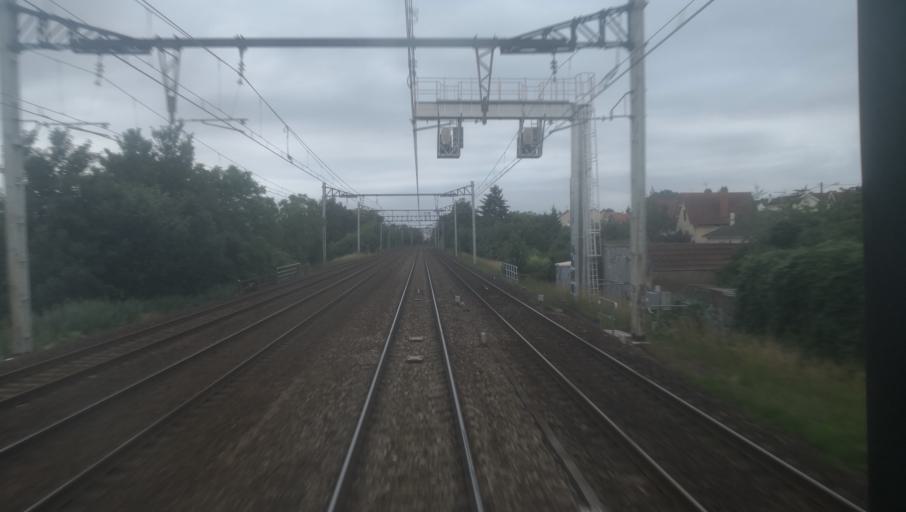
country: FR
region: Ile-de-France
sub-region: Departement de l'Essonne
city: Saint-Michel-sur-Orge
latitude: 48.6402
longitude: 2.3061
